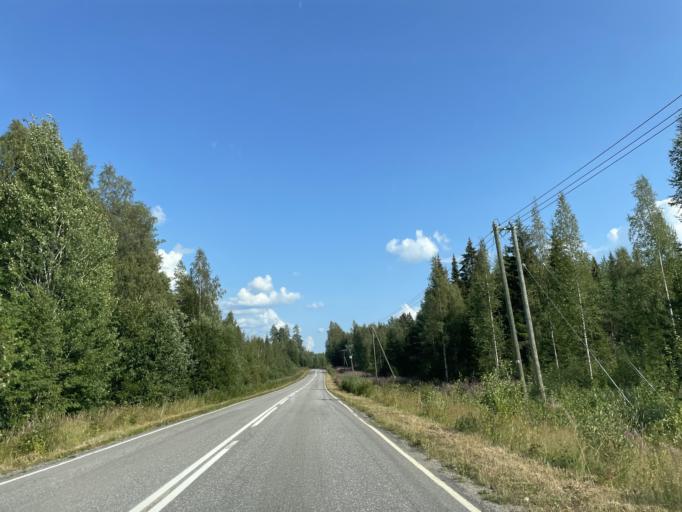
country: FI
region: Central Finland
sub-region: Saarijaervi-Viitasaari
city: Pihtipudas
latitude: 63.3536
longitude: 25.7754
